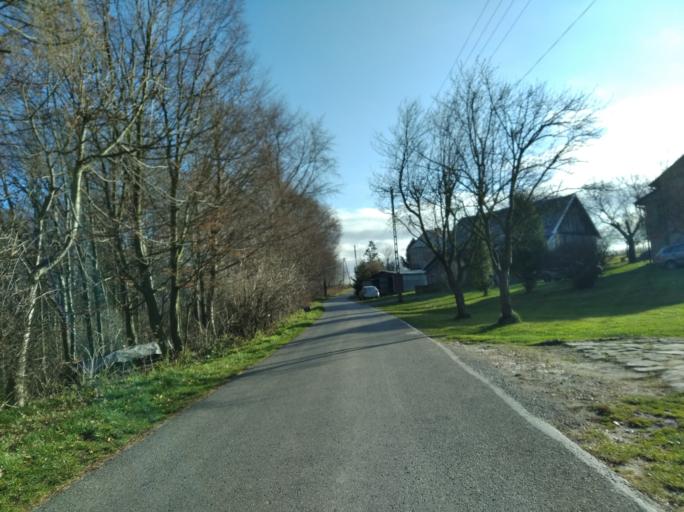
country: PL
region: Subcarpathian Voivodeship
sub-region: Powiat strzyzowski
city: Czudec
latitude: 49.9156
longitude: 21.8437
